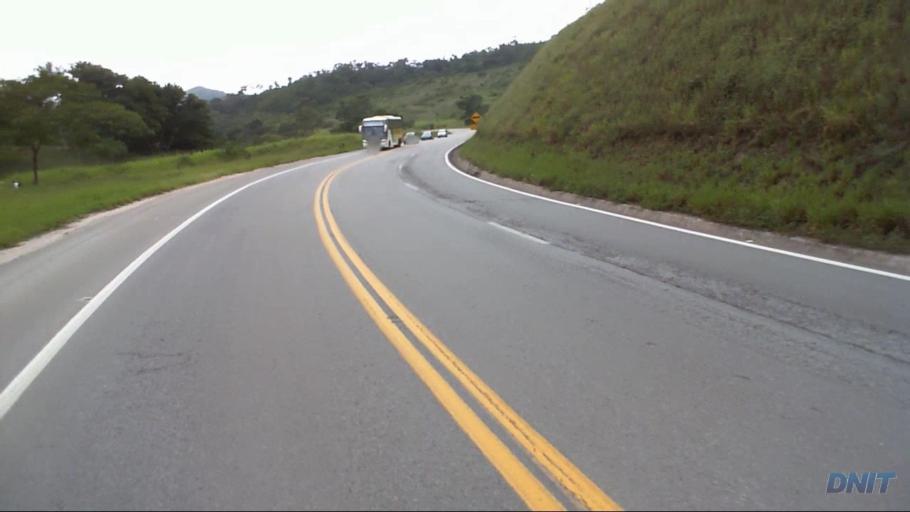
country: BR
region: Minas Gerais
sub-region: Nova Era
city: Nova Era
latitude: -19.6429
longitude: -42.9210
